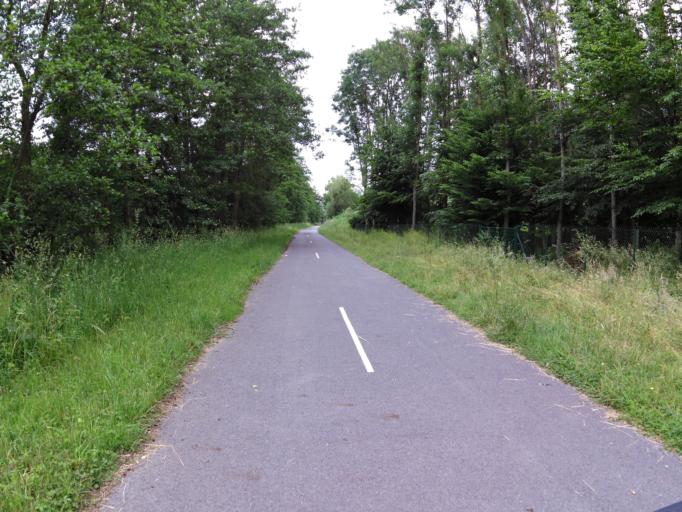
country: FR
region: Champagne-Ardenne
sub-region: Departement des Ardennes
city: Villers-Semeuse
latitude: 49.7560
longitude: 4.7336
